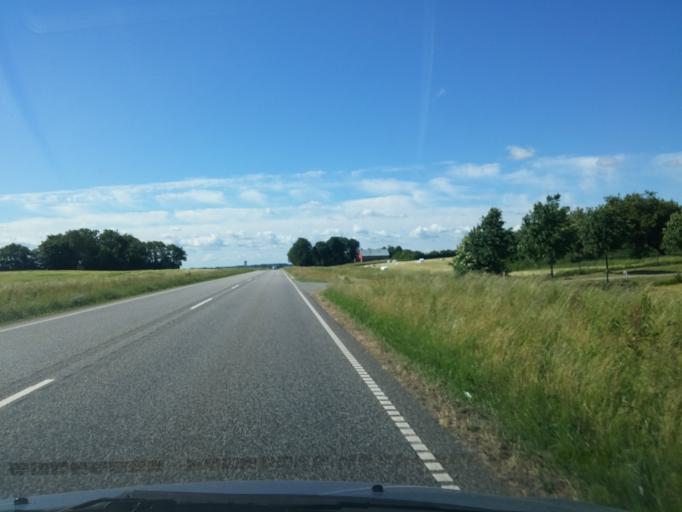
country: DK
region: South Denmark
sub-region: Haderslev Kommune
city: Haderslev
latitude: 55.2058
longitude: 9.4772
